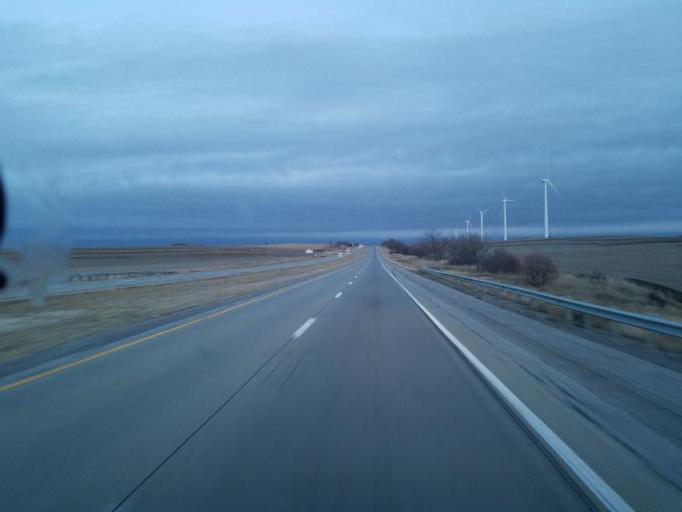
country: US
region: Iowa
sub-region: Pottawattamie County
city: Avoca
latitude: 41.4975
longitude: -95.1912
